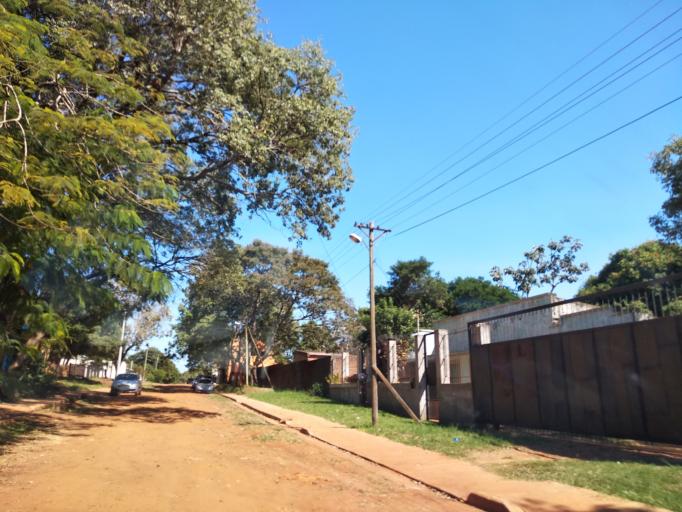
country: AR
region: Misiones
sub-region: Departamento de Capital
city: Posadas
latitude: -27.4262
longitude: -55.8847
